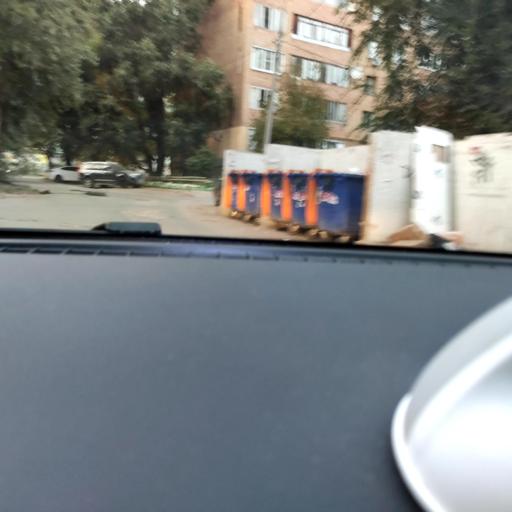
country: RU
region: Samara
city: Samara
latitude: 53.2330
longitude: 50.2588
